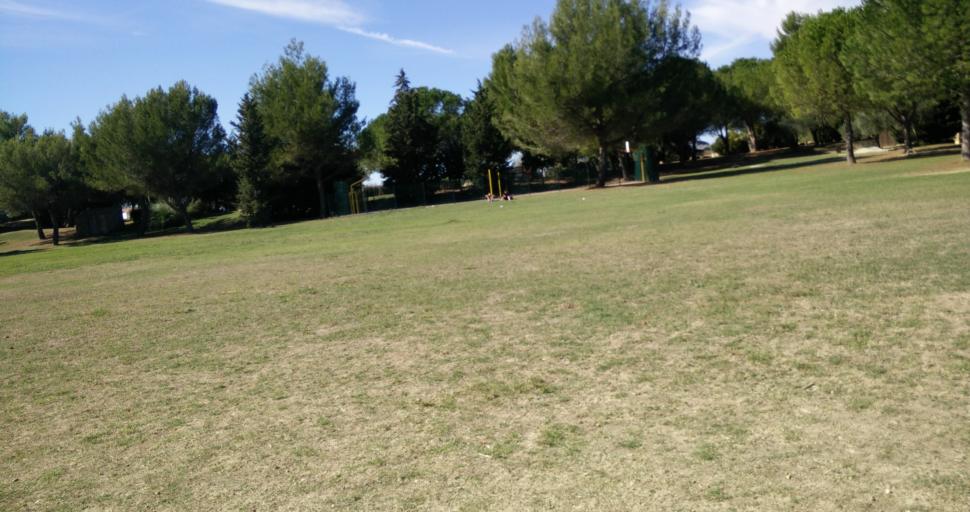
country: FR
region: Languedoc-Roussillon
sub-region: Departement du Gard
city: Codognan
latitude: 43.7293
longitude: 4.2153
